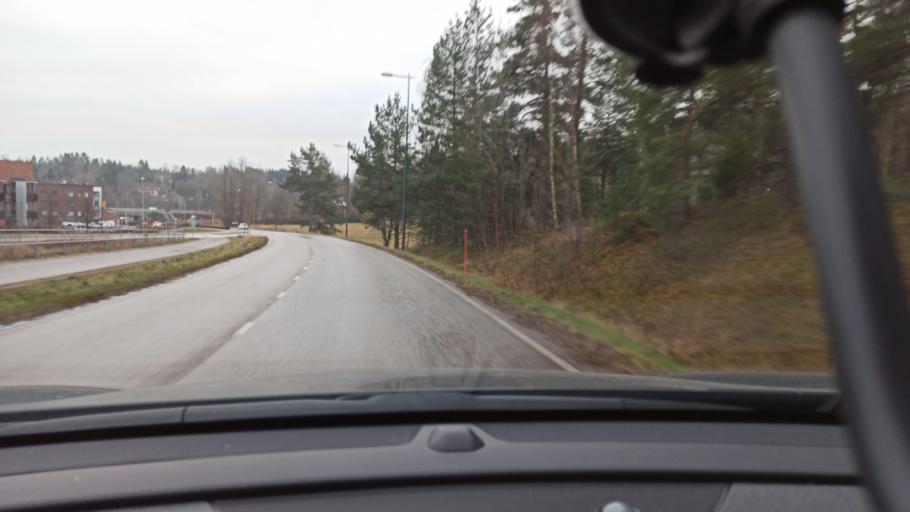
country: FI
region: Uusimaa
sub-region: Helsinki
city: Kirkkonummi
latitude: 60.1216
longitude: 24.4694
